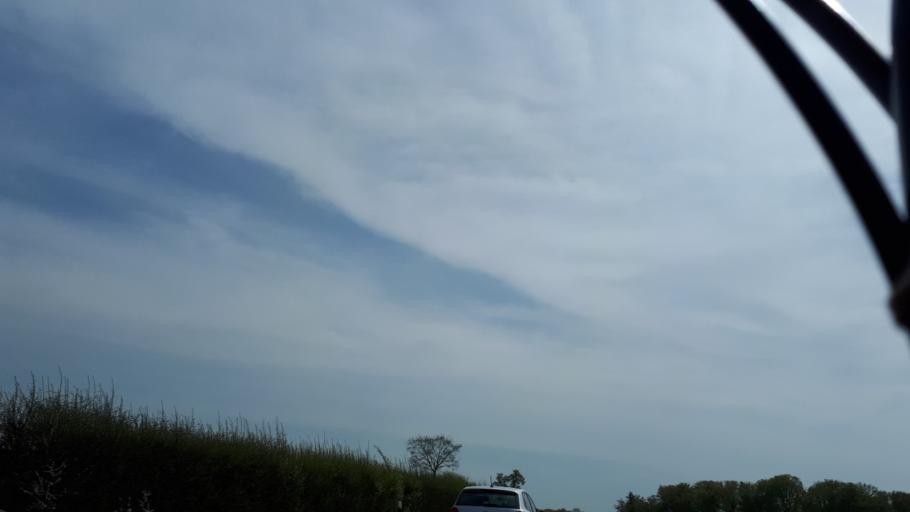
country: LU
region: Luxembourg
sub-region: Canton de Luxembourg
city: Bertrange
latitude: 49.5962
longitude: 6.0574
